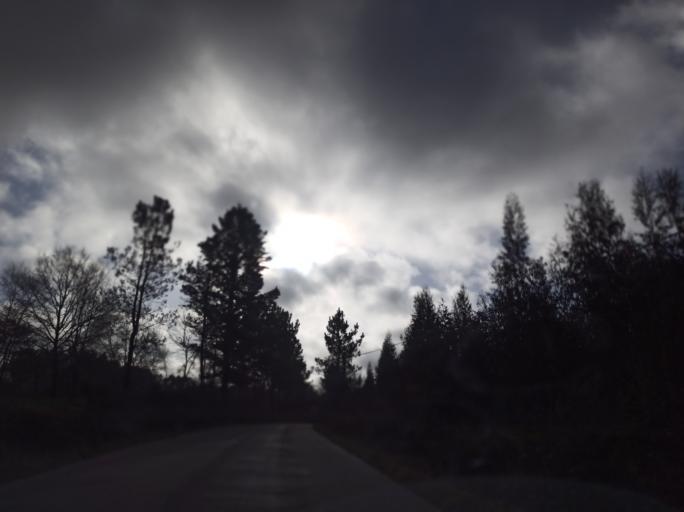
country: ES
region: Galicia
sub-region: Provincia da Coruna
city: Curtis
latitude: 43.0961
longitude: -7.9761
